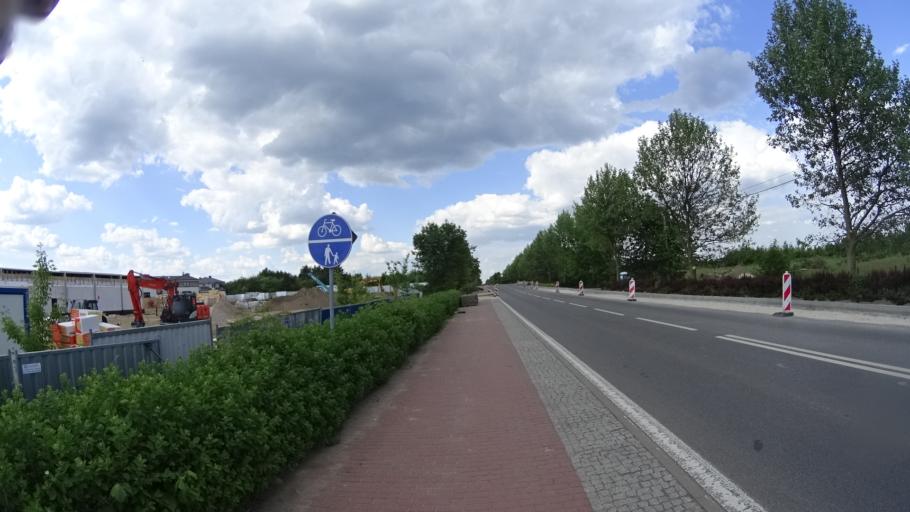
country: PL
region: Masovian Voivodeship
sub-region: Powiat piaseczynski
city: Tarczyn
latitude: 51.9895
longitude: 20.8380
